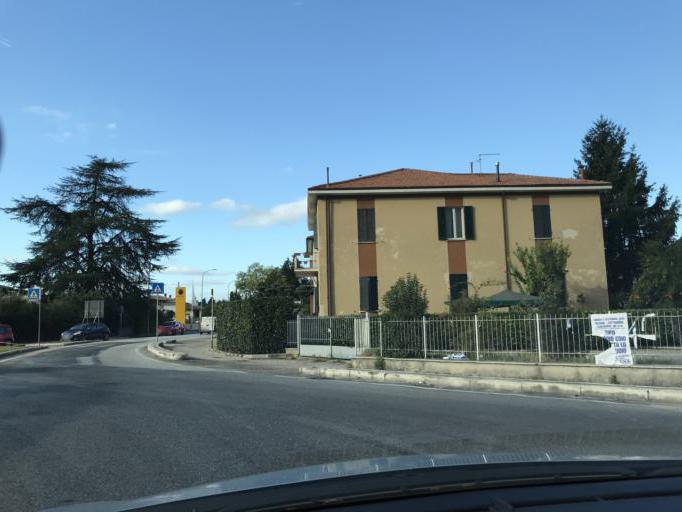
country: IT
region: Umbria
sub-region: Provincia di Perugia
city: Foligno
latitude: 42.9668
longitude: 12.6945
